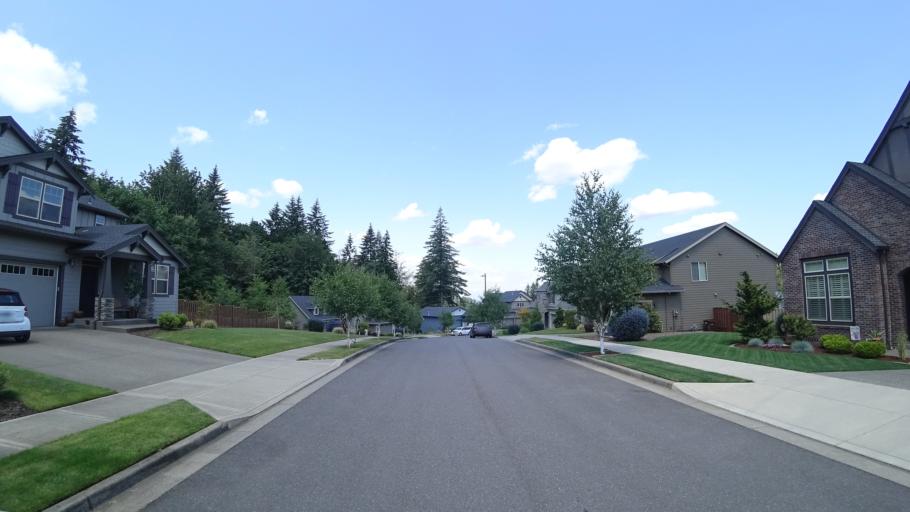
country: US
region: Oregon
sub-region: Clackamas County
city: Happy Valley
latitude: 45.4562
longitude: -122.5441
